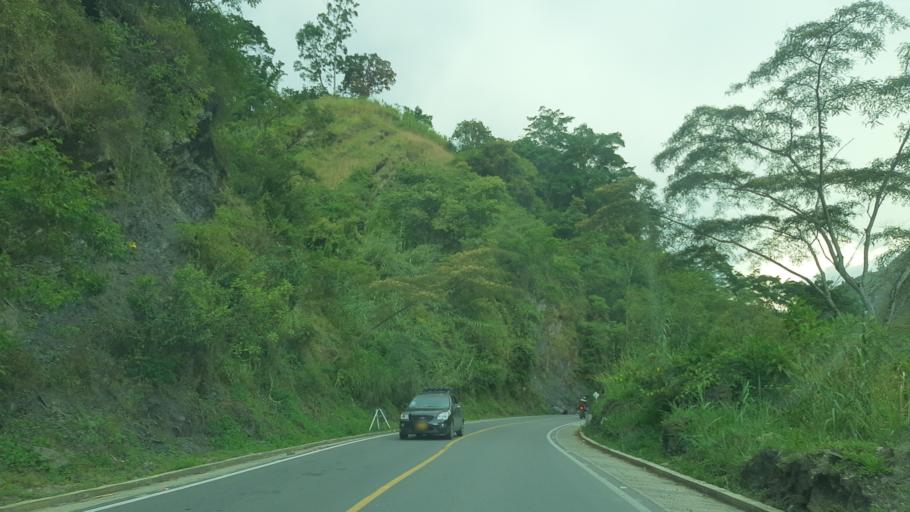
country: CO
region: Boyaca
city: Somondoco
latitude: 5.0092
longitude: -73.4116
